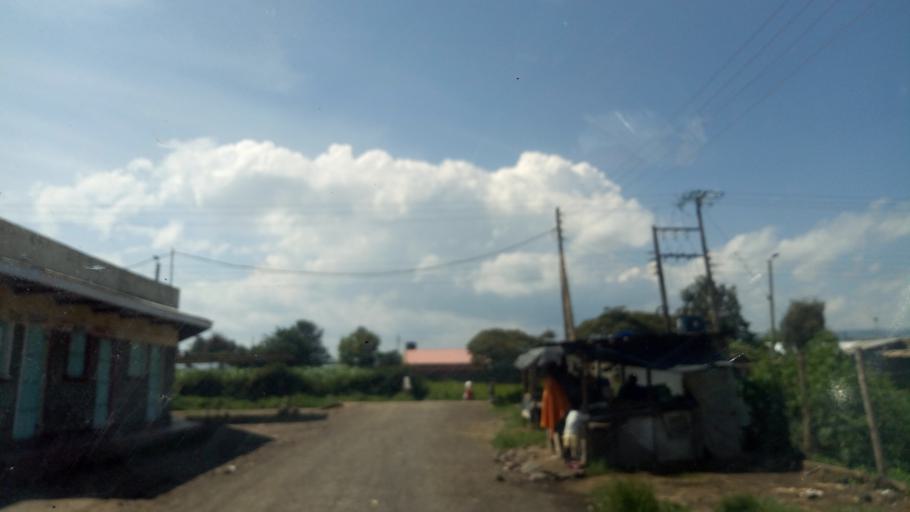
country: KE
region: Nakuru
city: Nakuru
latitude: -0.2776
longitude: 36.1182
